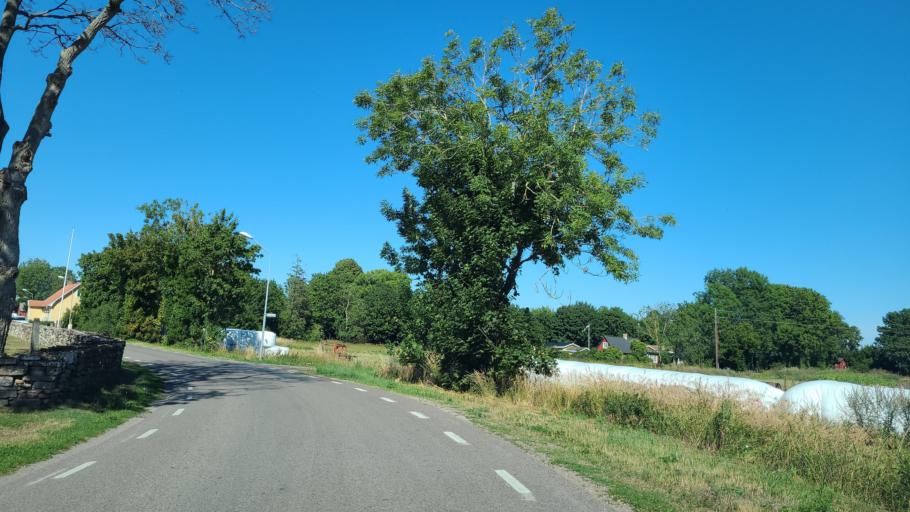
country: SE
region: Kalmar
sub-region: Borgholms Kommun
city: Borgholm
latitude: 56.8730
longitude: 16.8215
